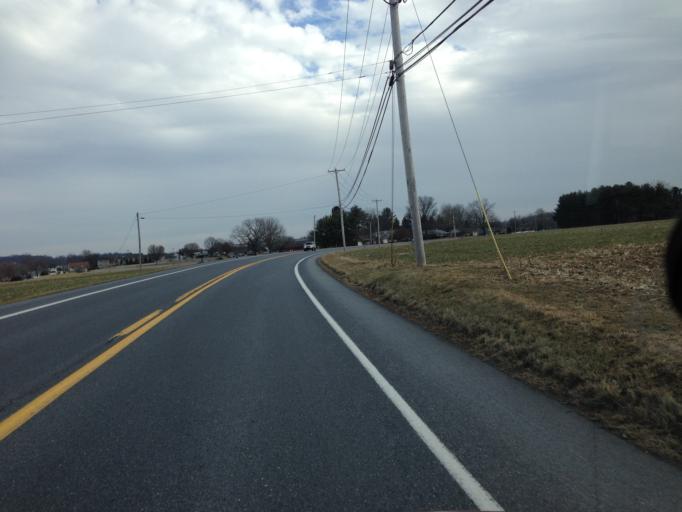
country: US
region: Pennsylvania
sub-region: Lancaster County
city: Lititz
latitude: 40.1698
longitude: -76.3226
